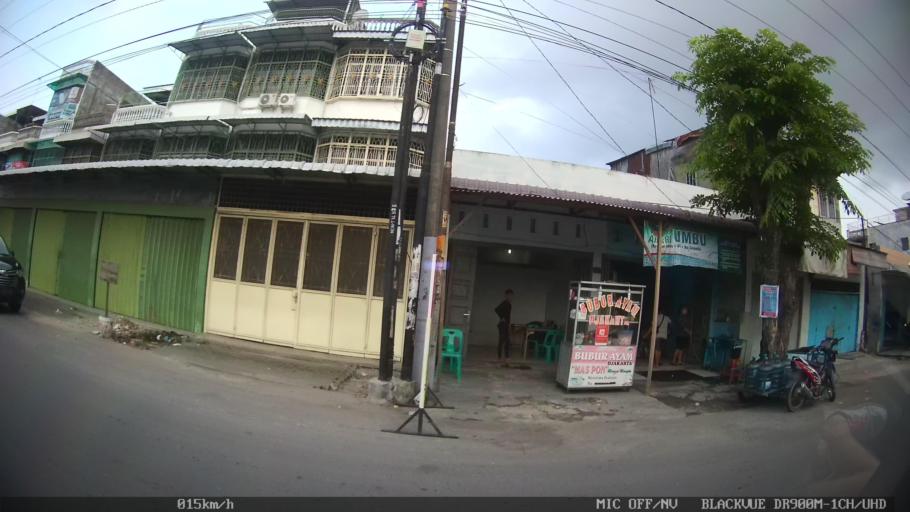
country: ID
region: North Sumatra
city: Medan
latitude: 3.5929
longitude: 98.7118
